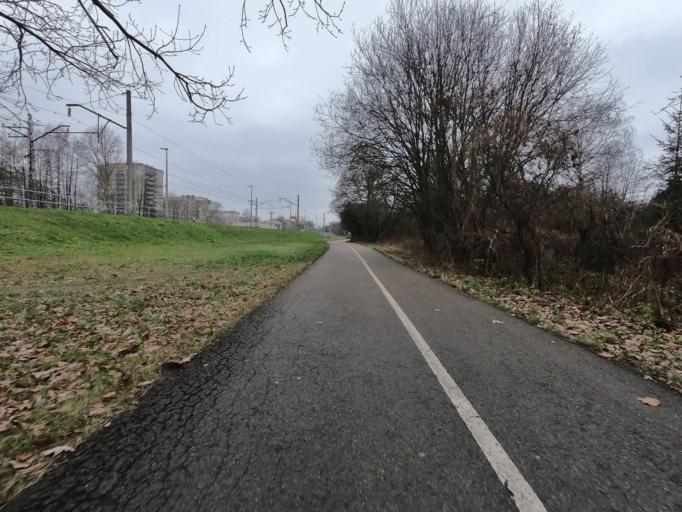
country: LV
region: Marupe
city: Marupe
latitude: 56.9491
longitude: 24.0248
